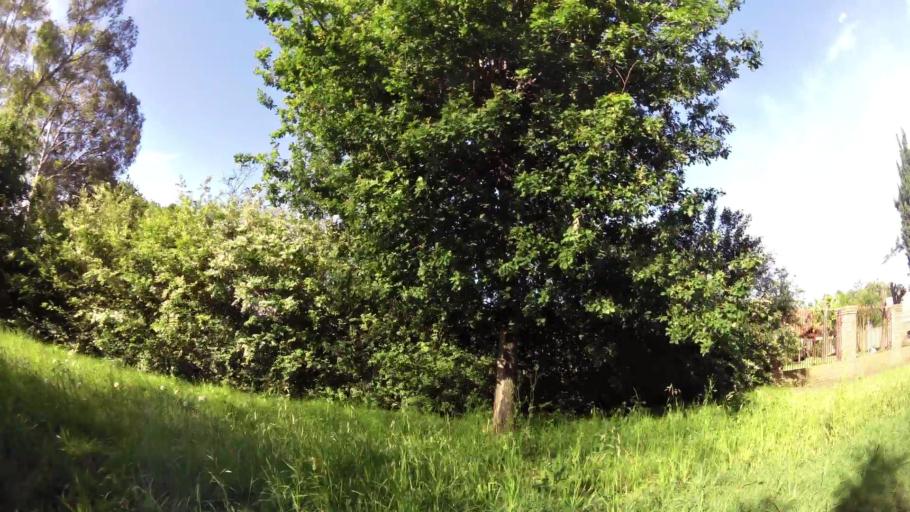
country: AR
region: Buenos Aires
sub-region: Partido de Quilmes
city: Quilmes
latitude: -34.8187
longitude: -58.2190
